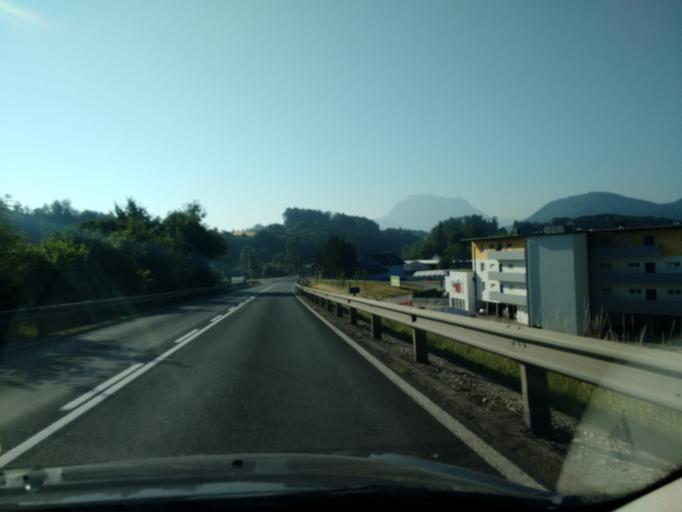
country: AT
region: Upper Austria
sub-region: Politischer Bezirk Gmunden
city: Altmunster
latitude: 47.9509
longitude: 13.7491
